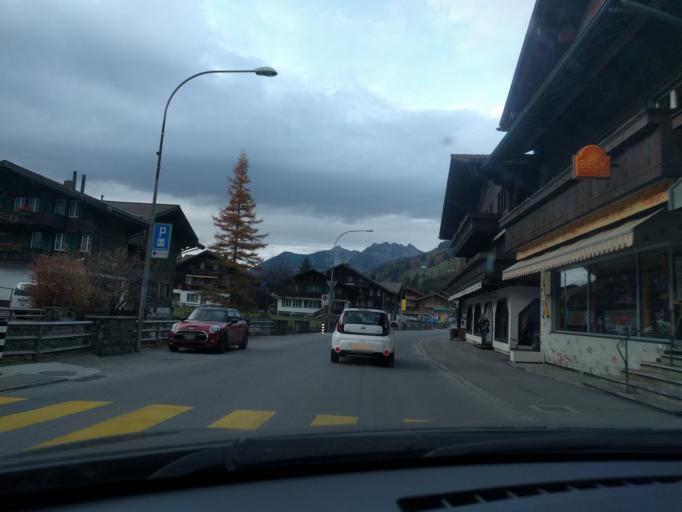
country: CH
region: Bern
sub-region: Obersimmental-Saanen District
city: Lenk
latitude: 46.4573
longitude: 7.4430
